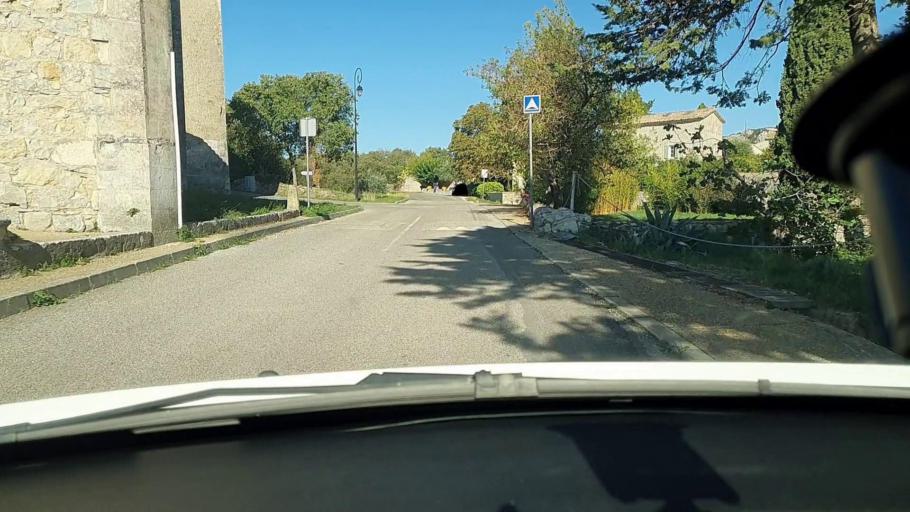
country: FR
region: Languedoc-Roussillon
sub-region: Departement du Gard
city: Barjac
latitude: 44.1855
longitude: 4.3275
